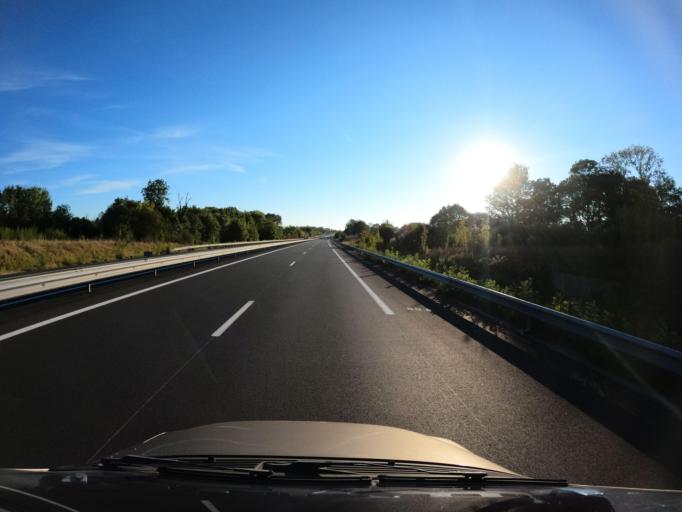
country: FR
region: Pays de la Loire
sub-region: Departement de la Vendee
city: Beaurepaire
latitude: 46.8838
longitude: -1.1047
